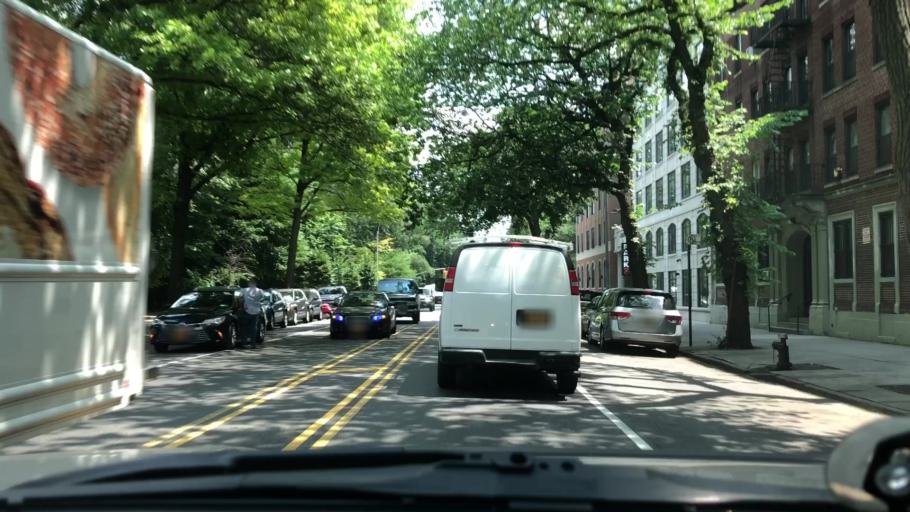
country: US
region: New York
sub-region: Kings County
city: Brooklyn
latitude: 40.6533
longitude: -73.9657
